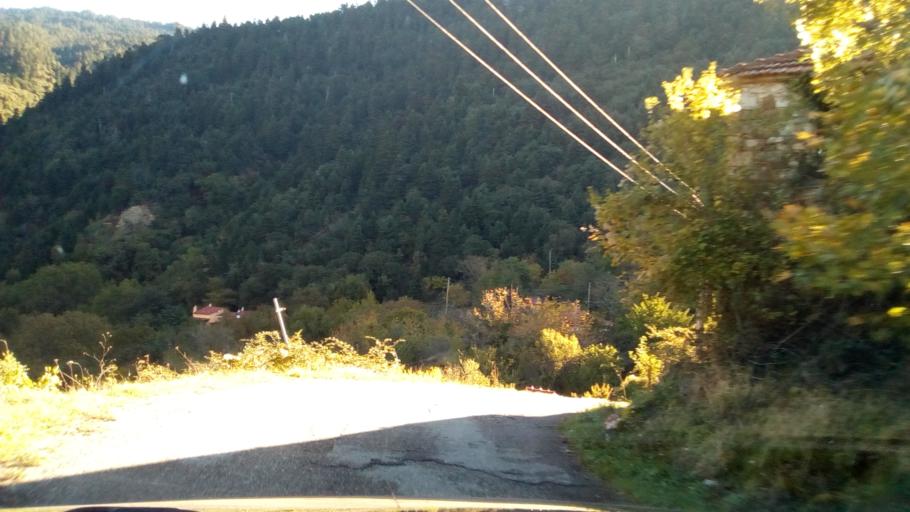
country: GR
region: West Greece
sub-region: Nomos Aitolias kai Akarnanias
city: Nafpaktos
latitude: 38.5625
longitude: 21.8537
